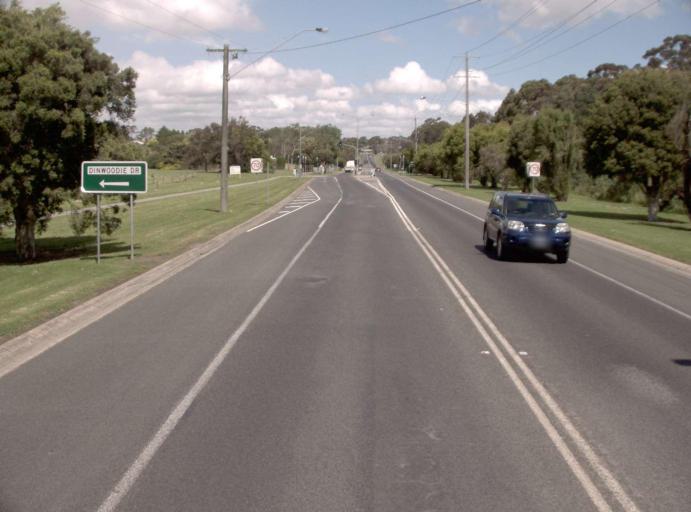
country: AU
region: Victoria
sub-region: Latrobe
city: Moe
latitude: -38.1806
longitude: 146.2728
